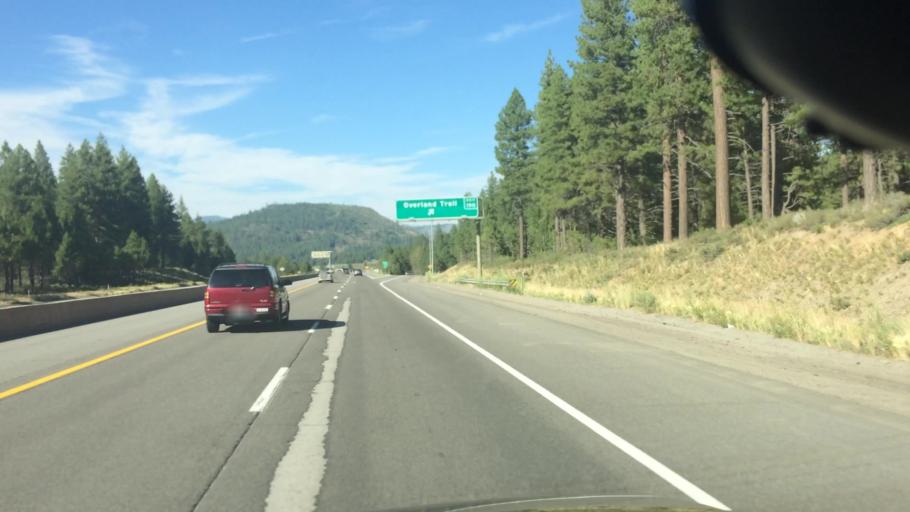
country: US
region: California
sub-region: Nevada County
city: Truckee
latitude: 39.3521
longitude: -120.1501
